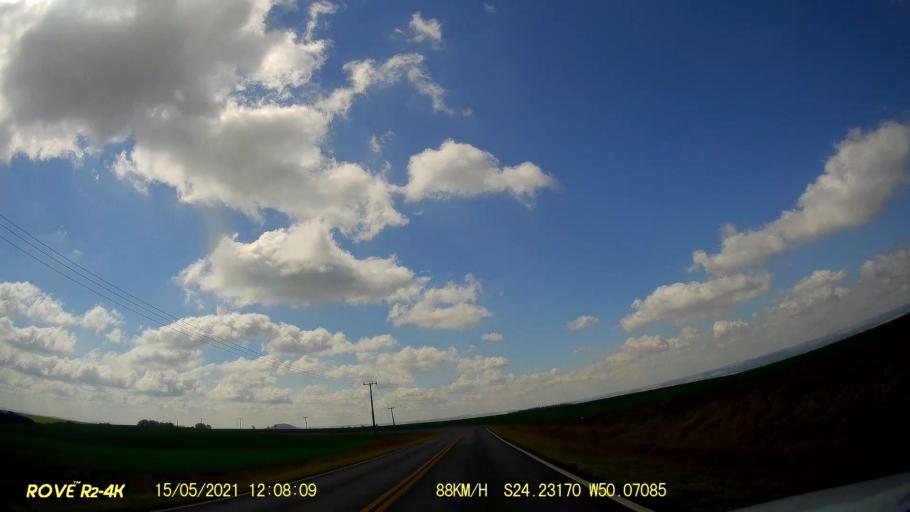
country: BR
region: Parana
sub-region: Pirai Do Sul
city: Pirai do Sul
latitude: -24.2316
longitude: -50.0709
